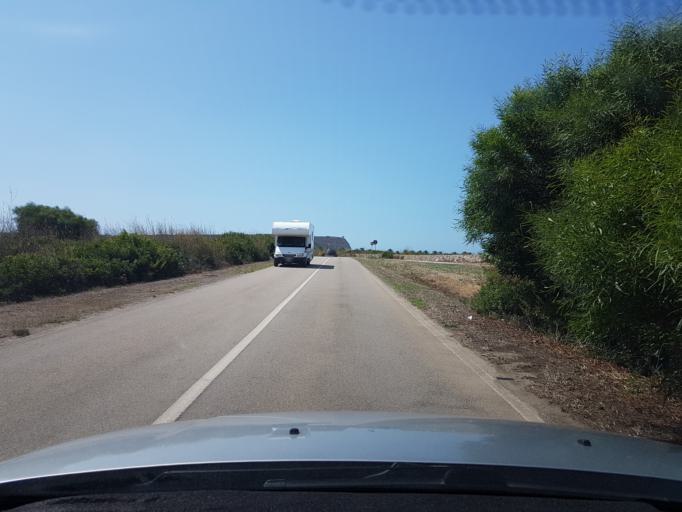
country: IT
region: Sardinia
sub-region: Provincia di Oristano
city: Riola Sardo
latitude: 40.0406
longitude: 8.4064
